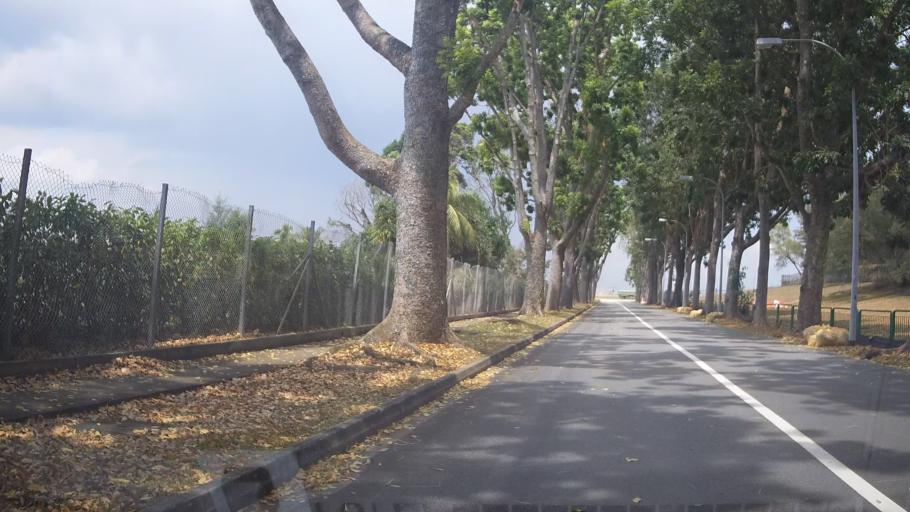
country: SG
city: Singapore
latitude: 1.3189
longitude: 103.9788
